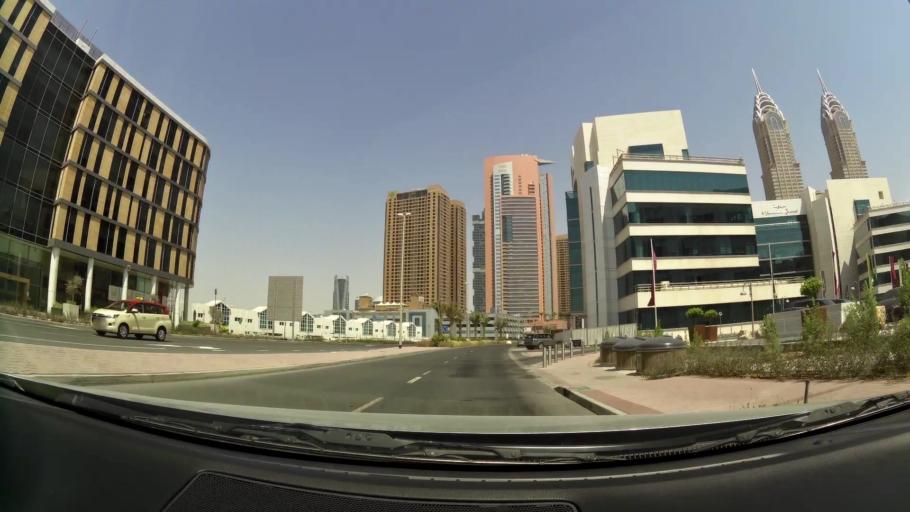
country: AE
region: Dubai
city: Dubai
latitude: 25.1044
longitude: 55.1680
